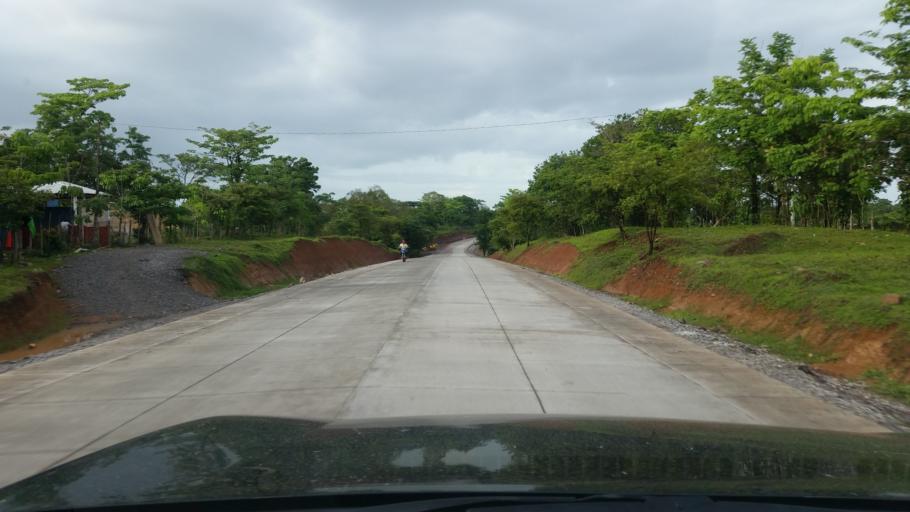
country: NI
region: Matagalpa
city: Rio Blanco
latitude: 13.1298
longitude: -85.0458
